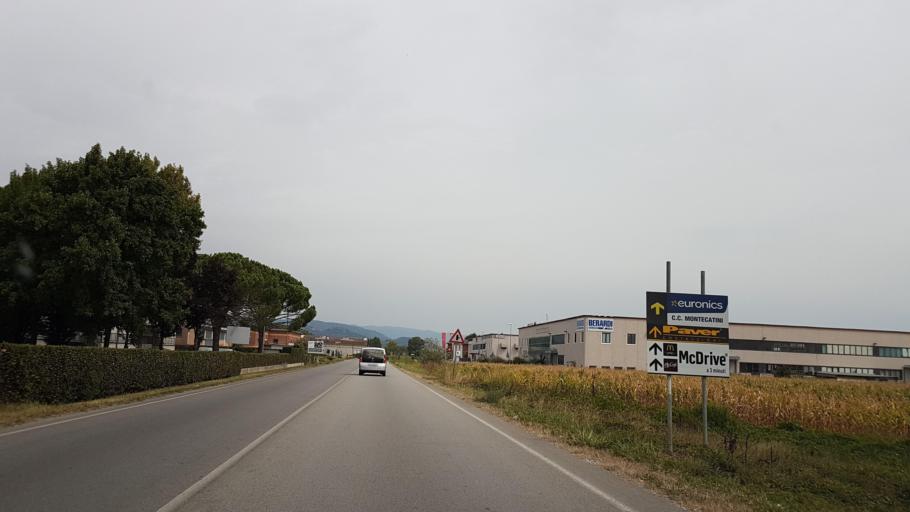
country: IT
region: Tuscany
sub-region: Provincia di Pistoia
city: Chiesina Uzzanese
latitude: 43.8443
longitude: 10.7268
